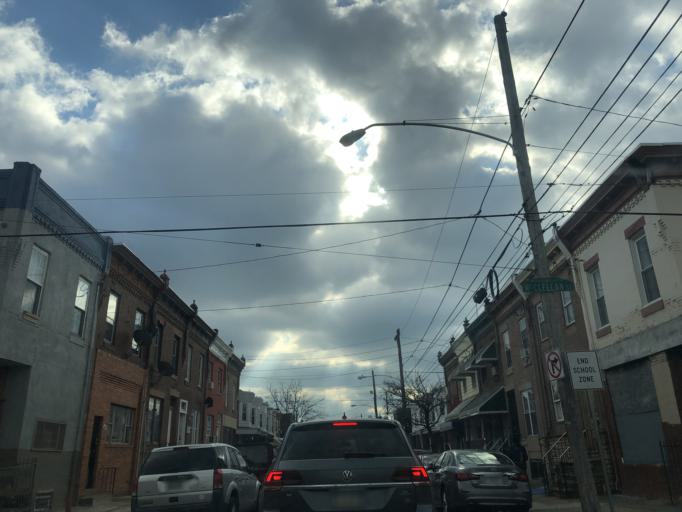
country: US
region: Pennsylvania
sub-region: Philadelphia County
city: Philadelphia
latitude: 39.9292
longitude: -75.1804
